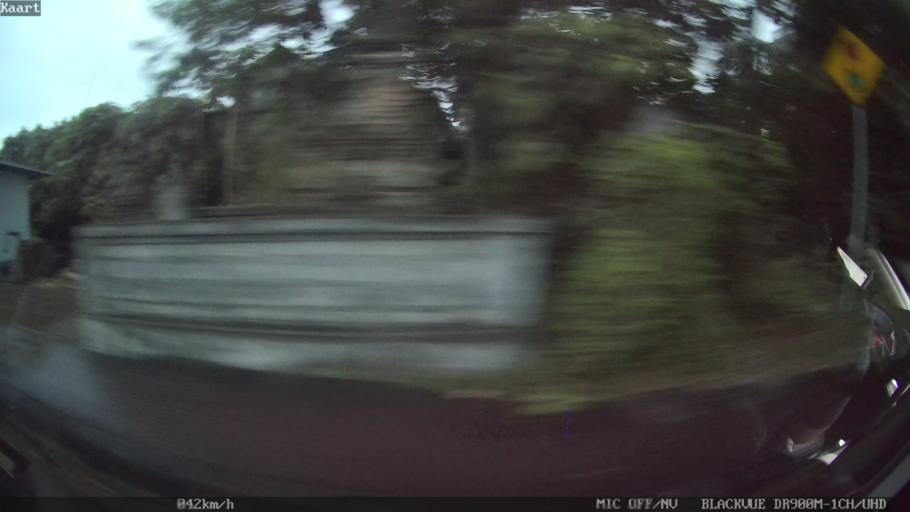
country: ID
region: Bali
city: Banjar Desa
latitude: -8.5830
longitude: 115.2783
